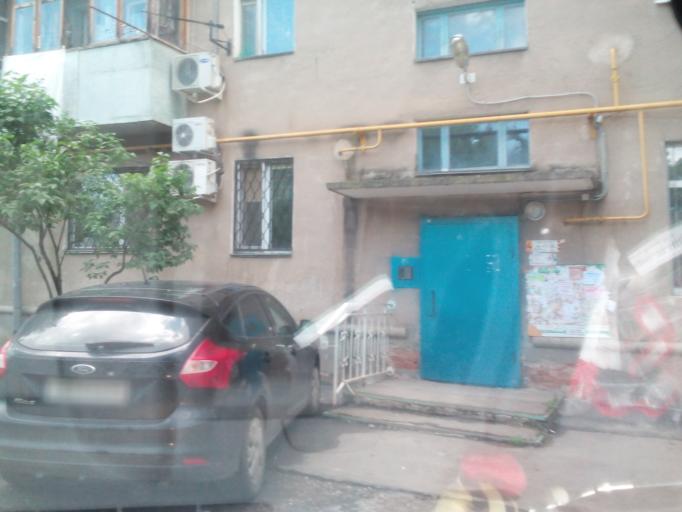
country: RU
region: Stavropol'skiy
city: Pyatigorsk
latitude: 44.0499
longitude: 43.0447
